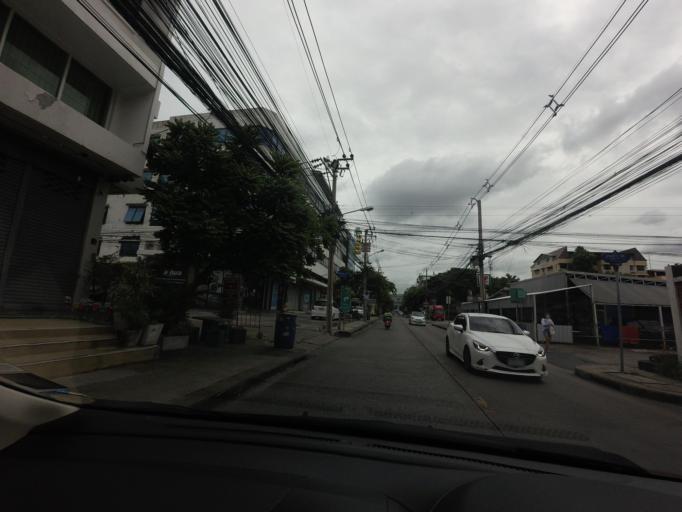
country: TH
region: Bangkok
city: Wang Thonglang
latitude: 13.7758
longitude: 100.6232
